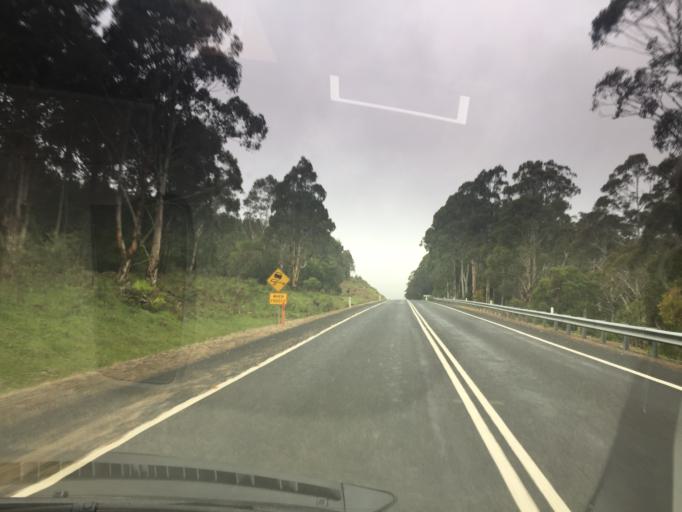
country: AU
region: New South Wales
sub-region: Bombala
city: Bombala
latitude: -36.6137
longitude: 149.3695
